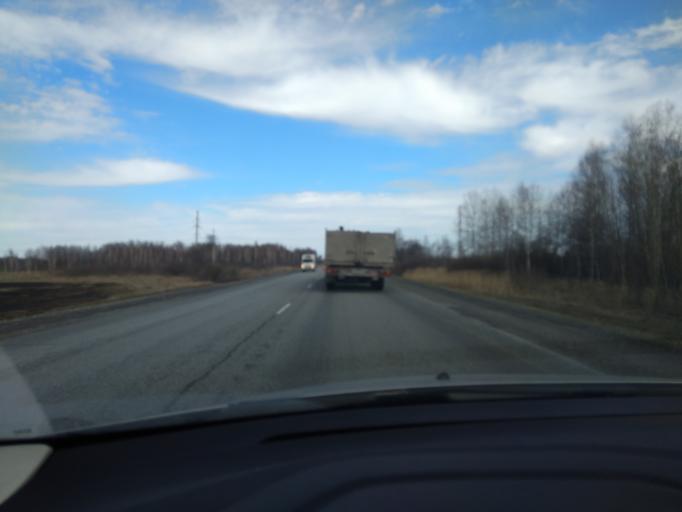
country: RU
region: Sverdlovsk
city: Pyshma
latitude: 56.9833
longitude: 63.2523
